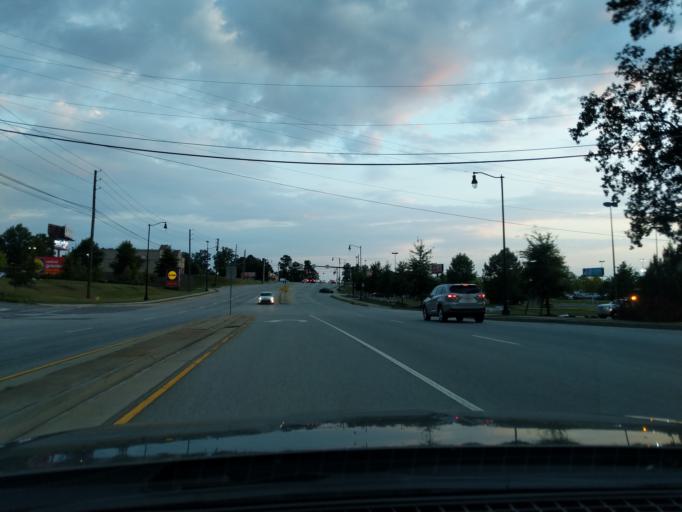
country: US
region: Georgia
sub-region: Columbia County
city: Martinez
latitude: 33.5124
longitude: -82.0273
